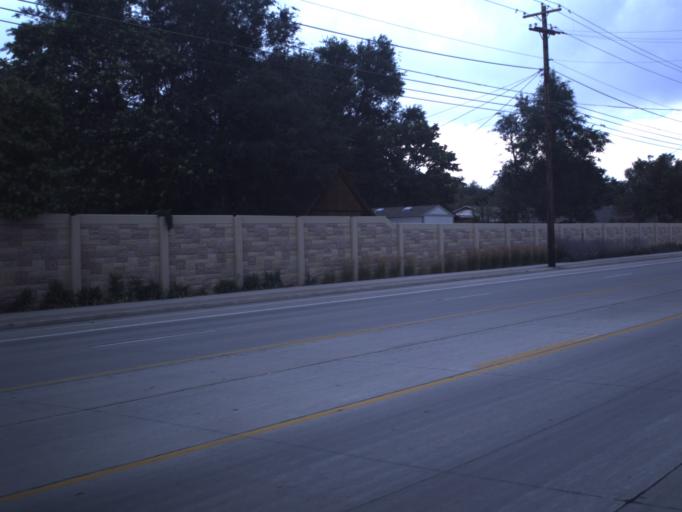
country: US
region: Utah
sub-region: Salt Lake County
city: White City
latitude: 40.5659
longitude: -111.8722
